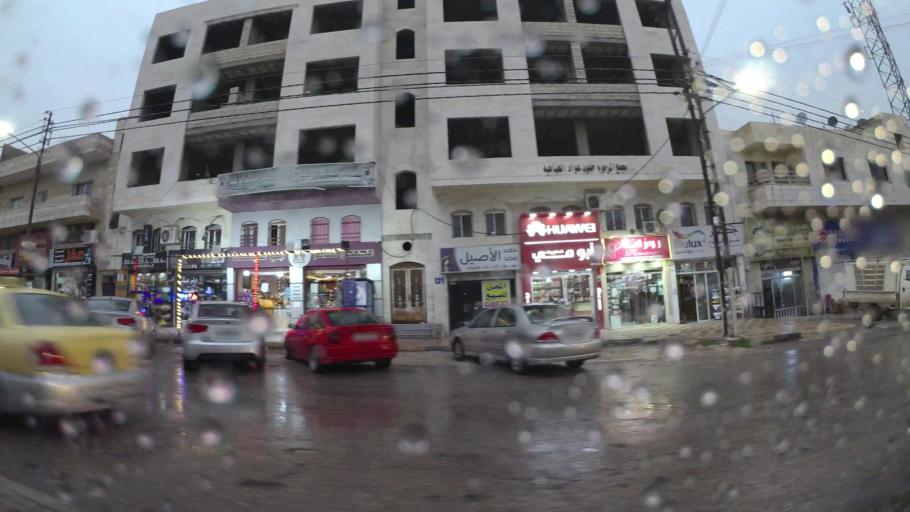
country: JO
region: Amman
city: Amman
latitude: 32.0018
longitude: 35.9682
